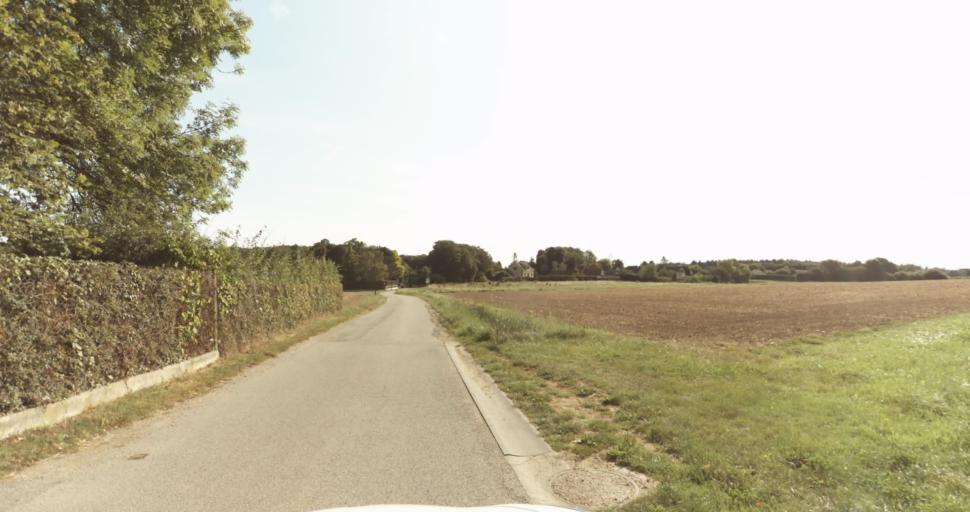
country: FR
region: Haute-Normandie
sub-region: Departement de l'Eure
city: Tillieres-sur-Avre
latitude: 48.7726
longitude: 1.0838
